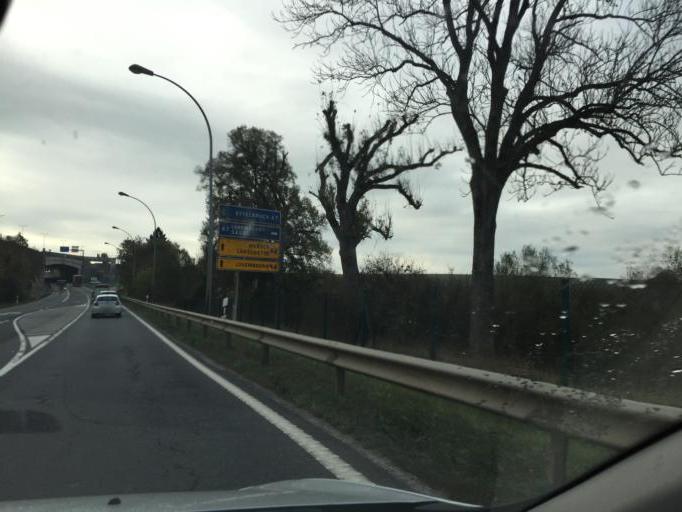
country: LU
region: Luxembourg
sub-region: Canton de Mersch
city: Mersch
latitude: 49.7656
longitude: 6.0887
